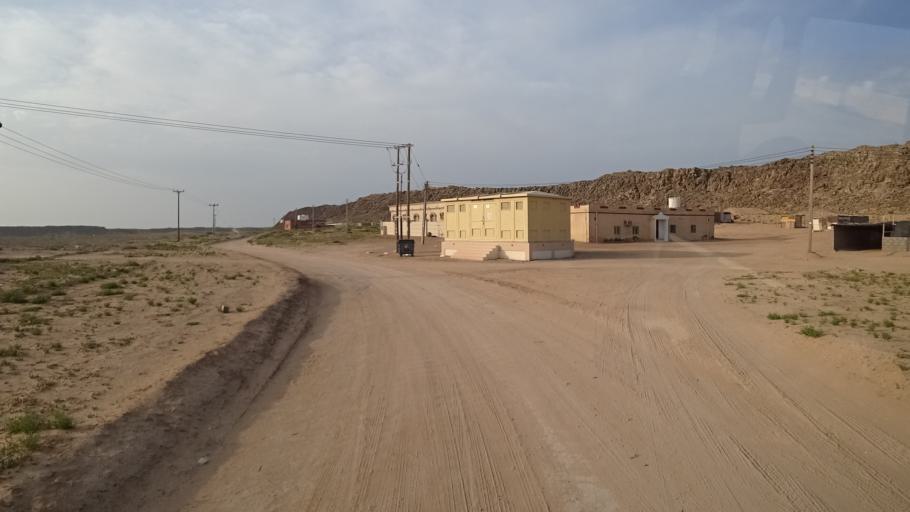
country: OM
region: Ash Sharqiyah
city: Sur
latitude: 22.4382
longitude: 59.8282
